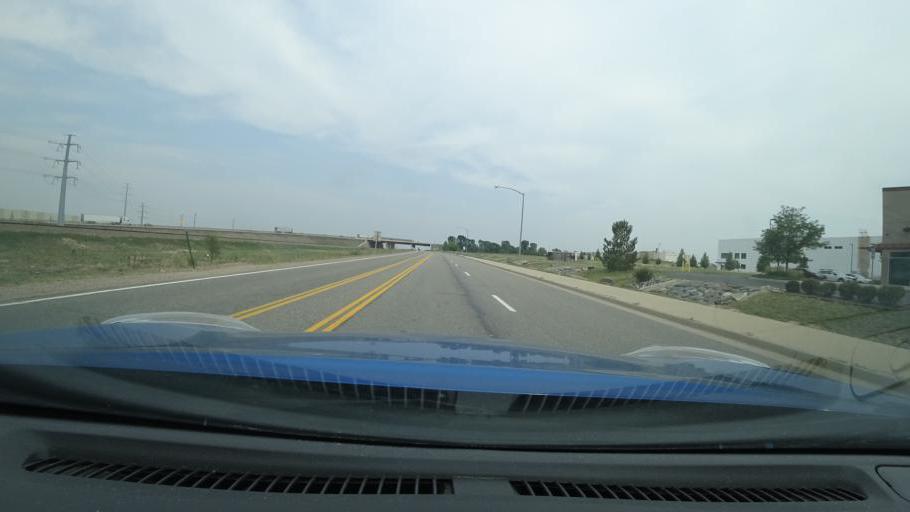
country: US
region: Colorado
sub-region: Adams County
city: Aurora
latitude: 39.7526
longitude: -104.7584
